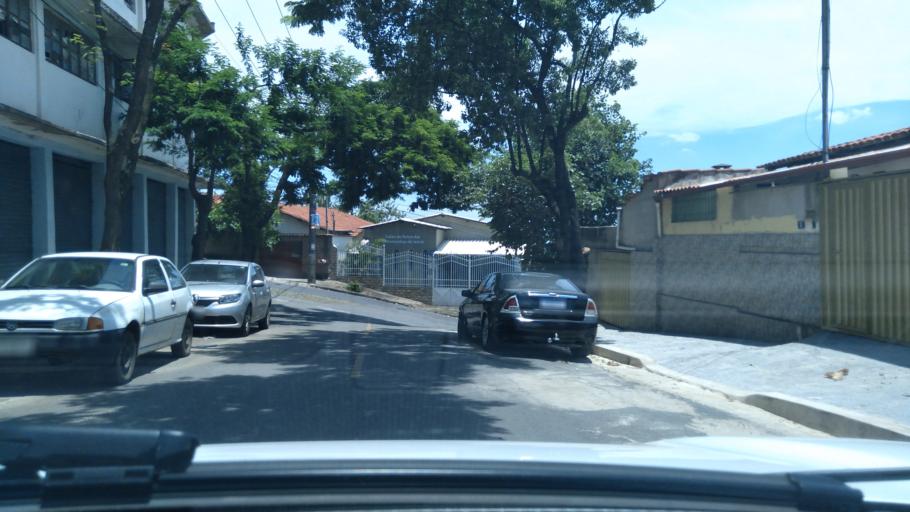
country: BR
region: Minas Gerais
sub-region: Contagem
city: Contagem
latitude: -19.9253
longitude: -44.0153
